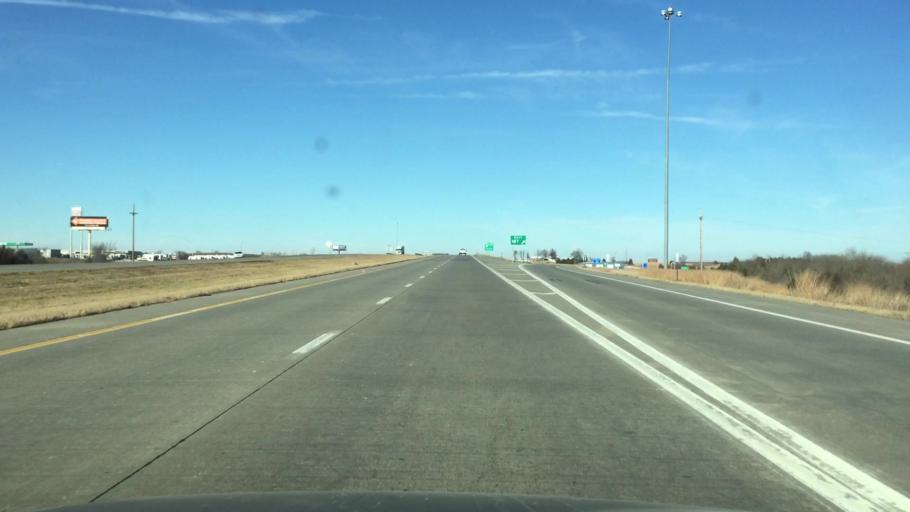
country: US
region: Kansas
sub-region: Franklin County
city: Ottawa
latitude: 38.6190
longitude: -95.2322
